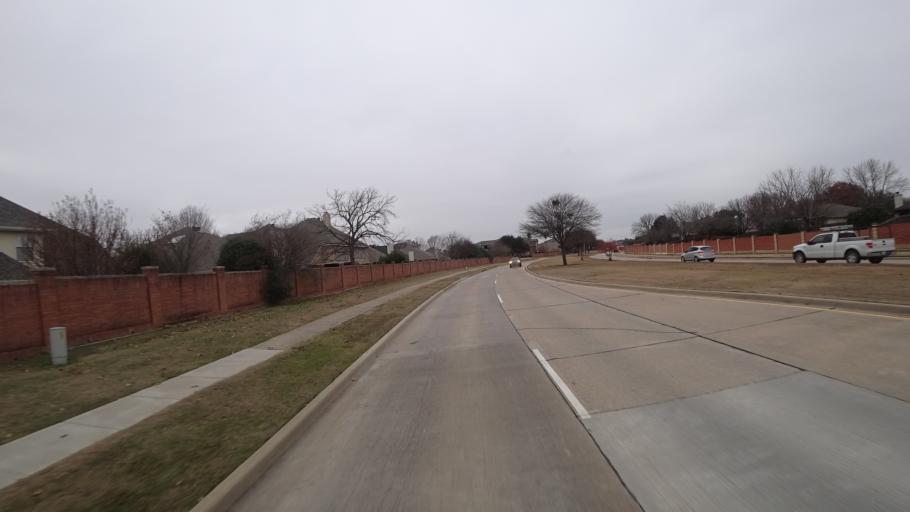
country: US
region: Texas
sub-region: Denton County
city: Lewisville
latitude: 33.0581
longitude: -97.0286
